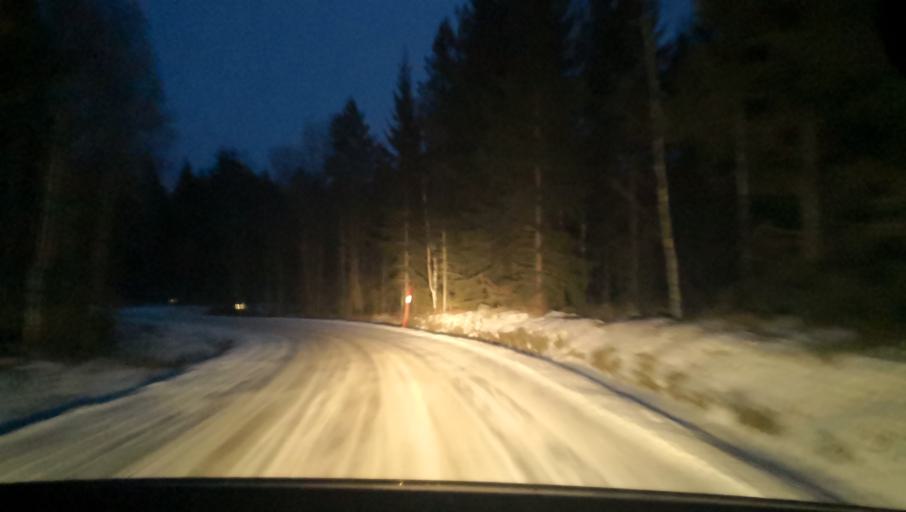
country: SE
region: Uppsala
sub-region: Heby Kommun
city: Tarnsjo
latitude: 60.2530
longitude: 16.7477
